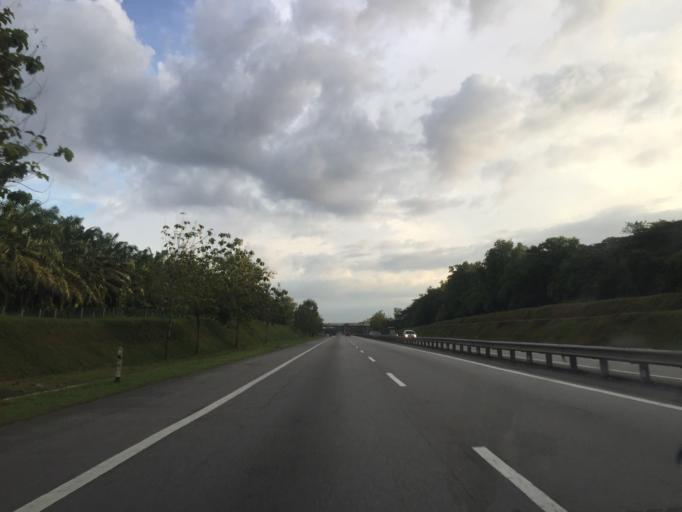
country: MY
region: Kedah
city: Bedong
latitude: 5.7669
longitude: 100.5047
